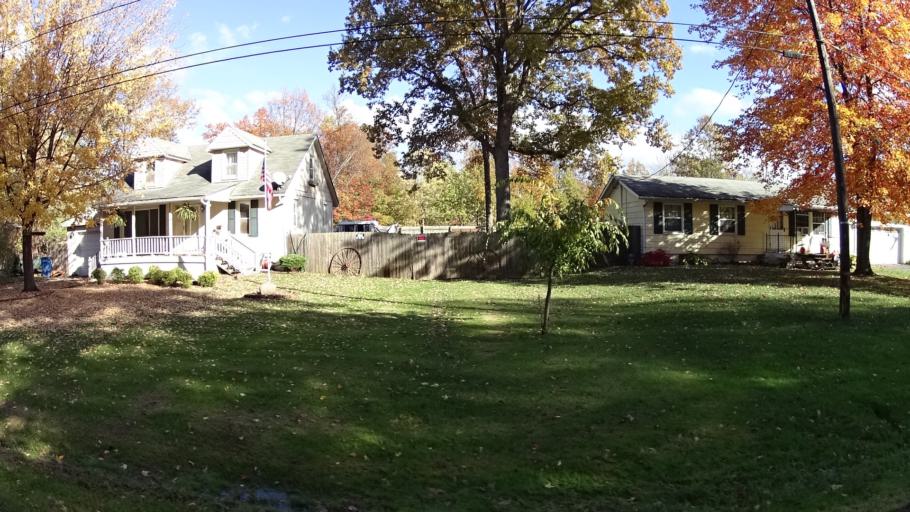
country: US
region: Ohio
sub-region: Lorain County
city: Lorain
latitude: 41.4342
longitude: -82.1411
